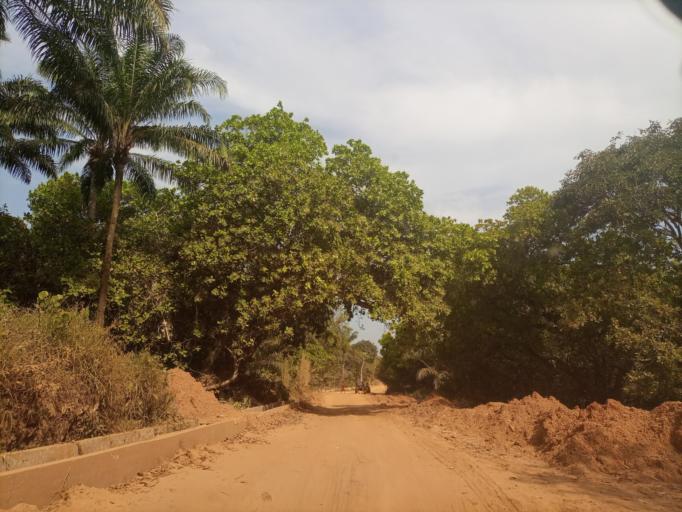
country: NG
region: Enugu
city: Opi
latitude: 6.8103
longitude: 7.5234
